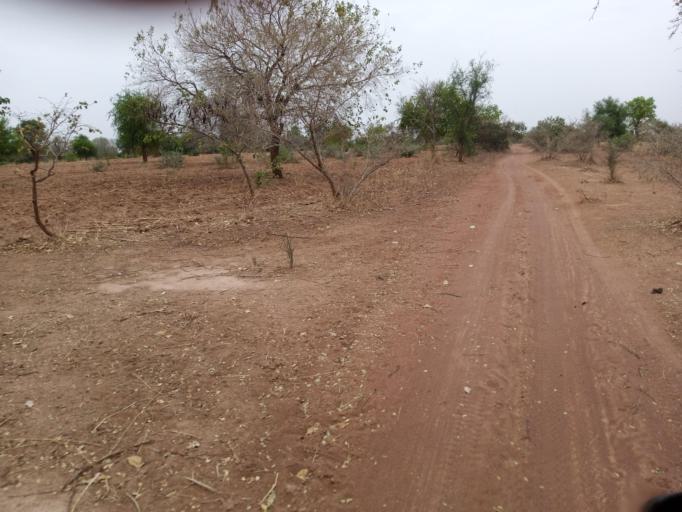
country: BF
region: Boucle du Mouhoun
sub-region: Province de la Kossi
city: Nouna
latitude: 12.8363
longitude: -4.0770
